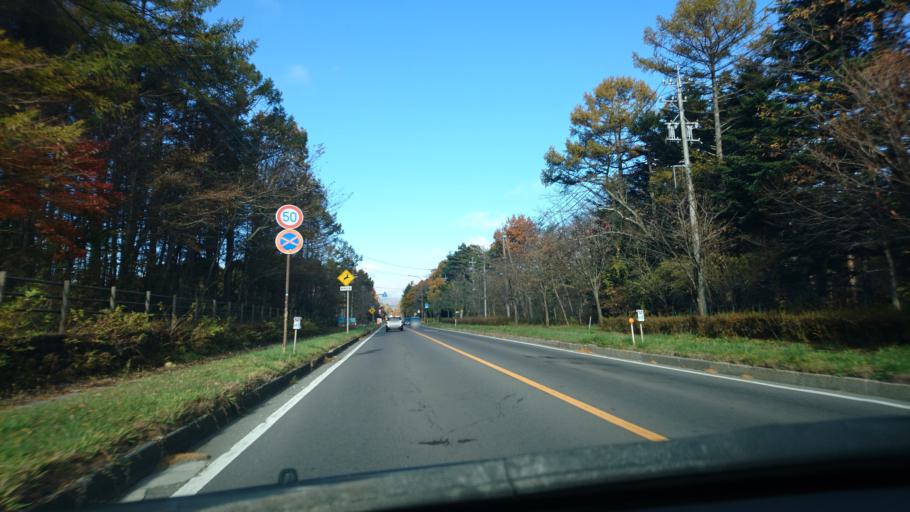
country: JP
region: Nagano
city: Saku
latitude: 36.3246
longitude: 138.6218
